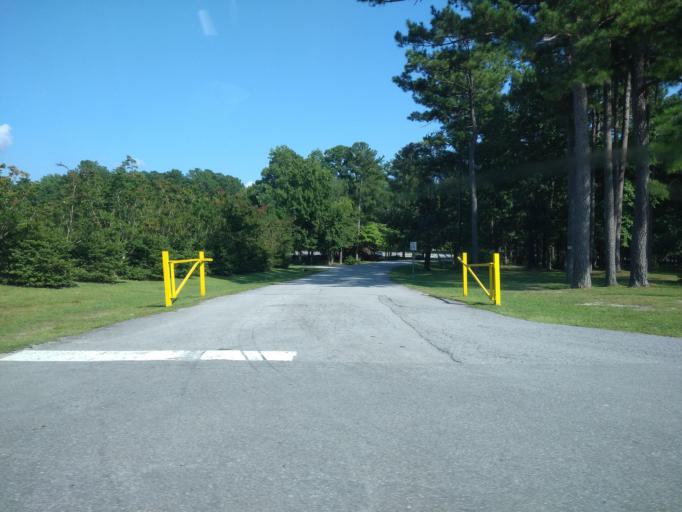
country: US
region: North Carolina
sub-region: Onslow County
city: Pumpkin Center
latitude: 34.7483
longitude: -77.3589
